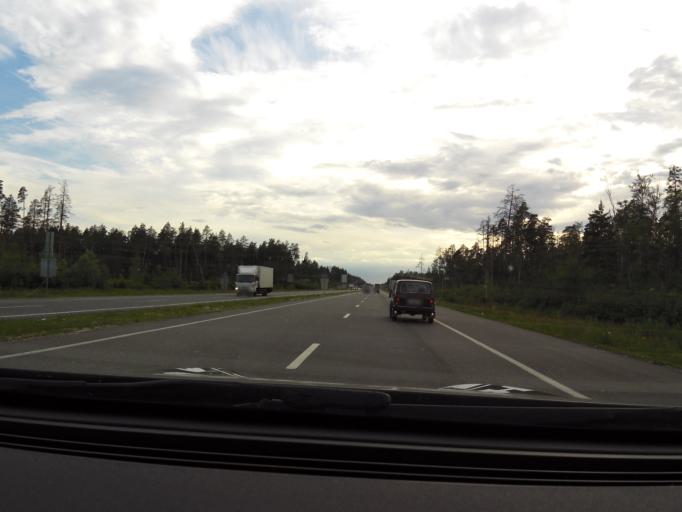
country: RU
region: Vladimir
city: Orgtrud
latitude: 56.1032
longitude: 40.6197
